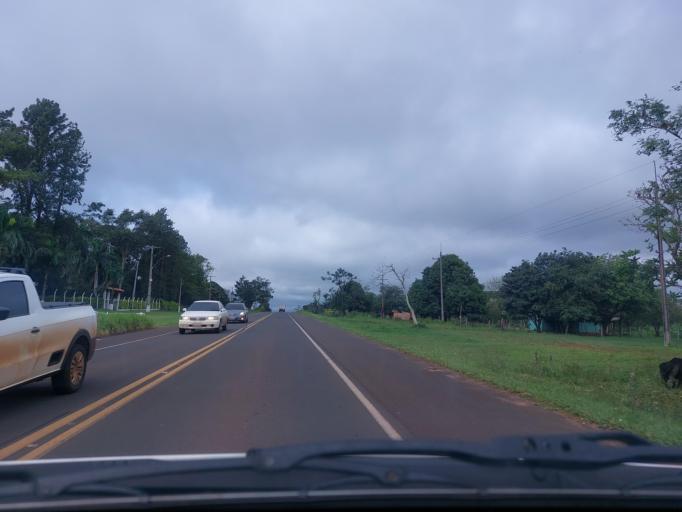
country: PY
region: San Pedro
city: Guayaybi
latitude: -24.6074
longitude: -56.3825
